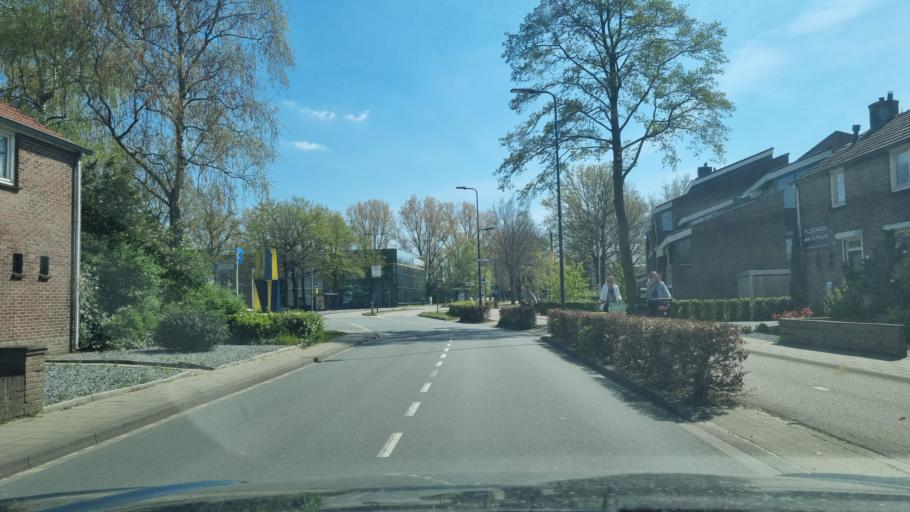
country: NL
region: North Brabant
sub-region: Gemeente 's-Hertogenbosch
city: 's-Hertogenbosch
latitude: 51.7165
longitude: 5.3689
